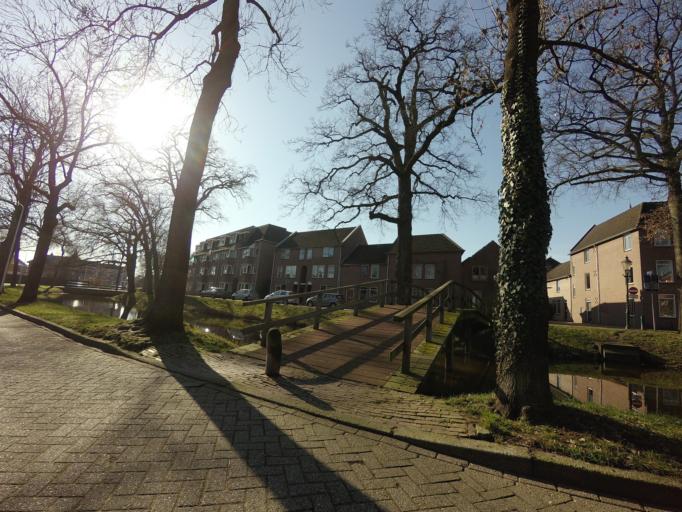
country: NL
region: Gelderland
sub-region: Gemeente Lochem
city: Lochem
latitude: 52.1617
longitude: 6.4187
